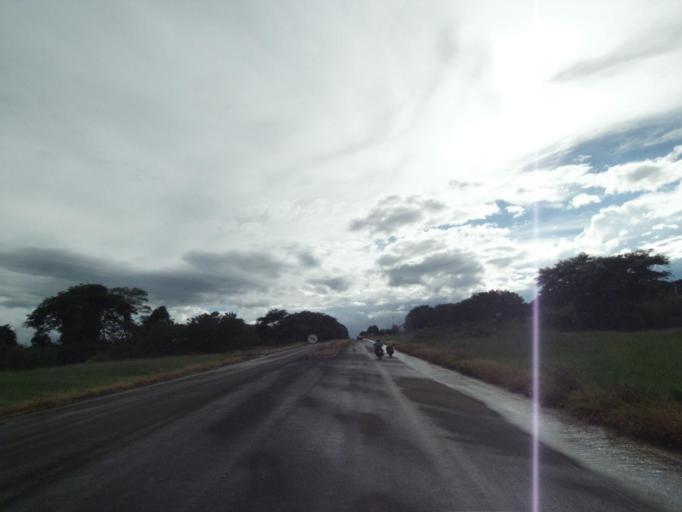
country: BR
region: Goias
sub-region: Itaberai
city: Itaberai
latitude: -15.9188
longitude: -49.5969
